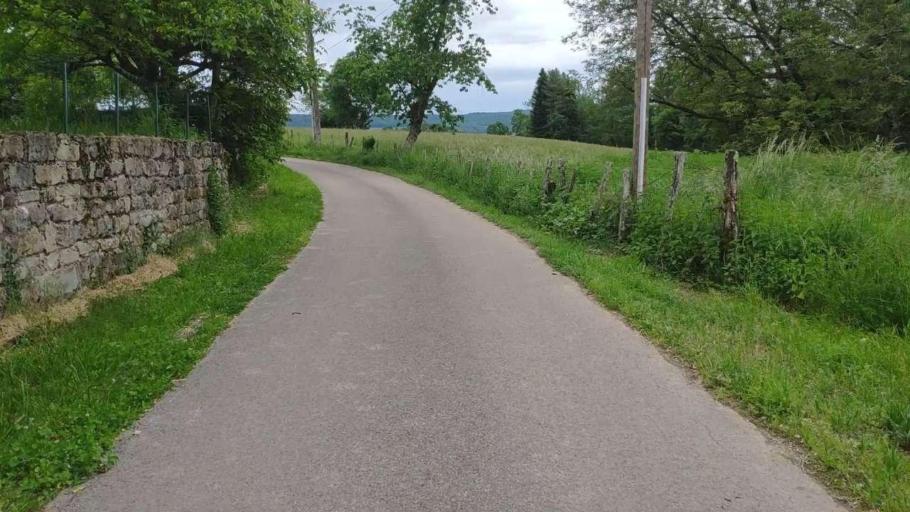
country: FR
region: Franche-Comte
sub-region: Departement du Jura
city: Perrigny
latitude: 46.7540
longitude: 5.5739
